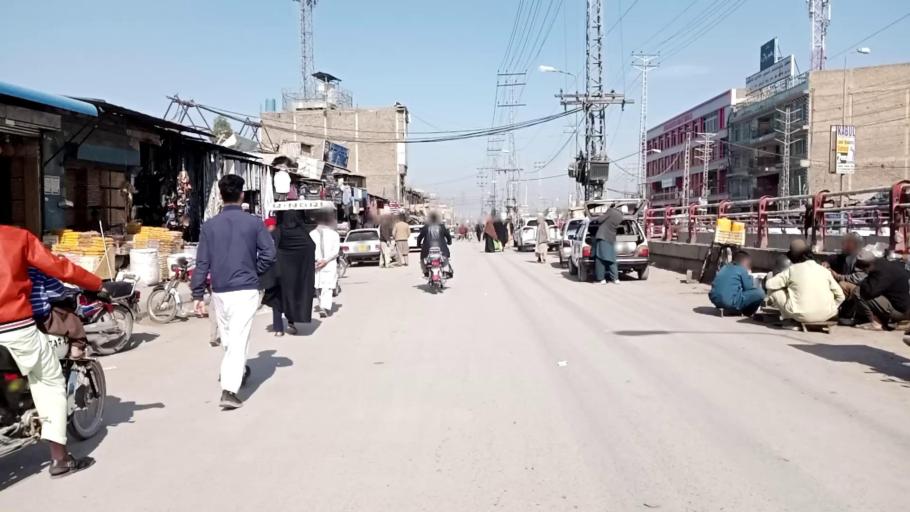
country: PK
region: Khyber Pakhtunkhwa
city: Peshawar
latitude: 33.9962
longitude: 71.4699
